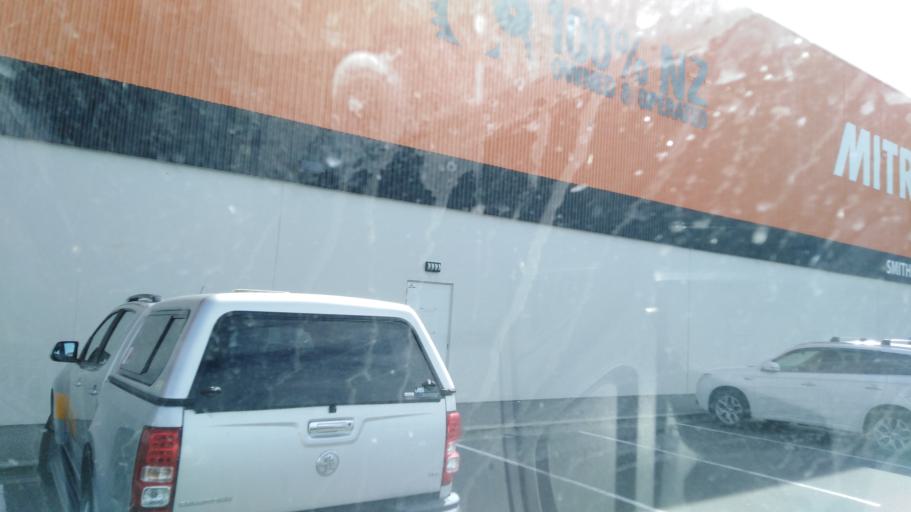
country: NZ
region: Canterbury
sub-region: Selwyn District
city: Prebbleton
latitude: -43.5422
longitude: 172.5276
